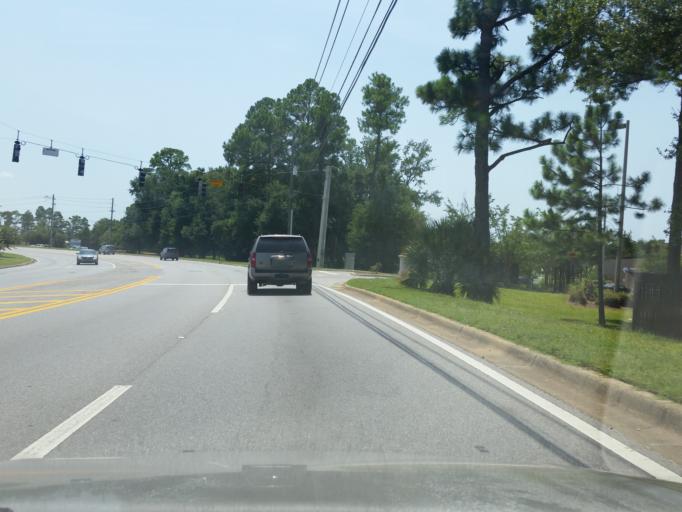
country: US
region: Florida
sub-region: Escambia County
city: Brent
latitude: 30.4846
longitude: -87.2603
